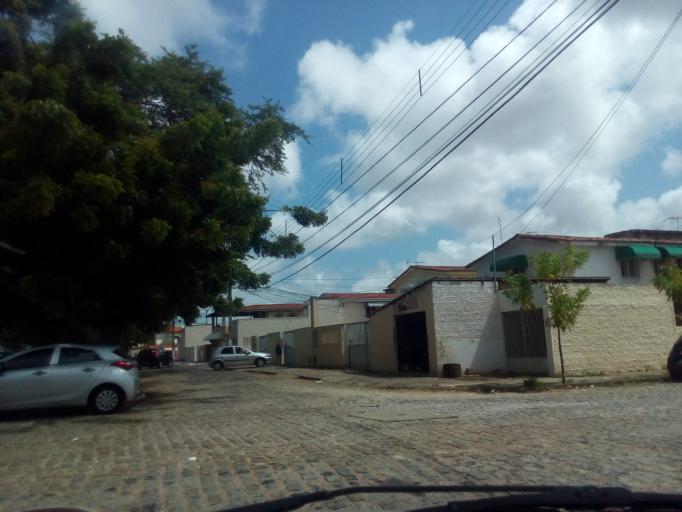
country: BR
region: Rio Grande do Norte
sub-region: Natal
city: Natal
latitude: -5.8498
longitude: -35.2018
